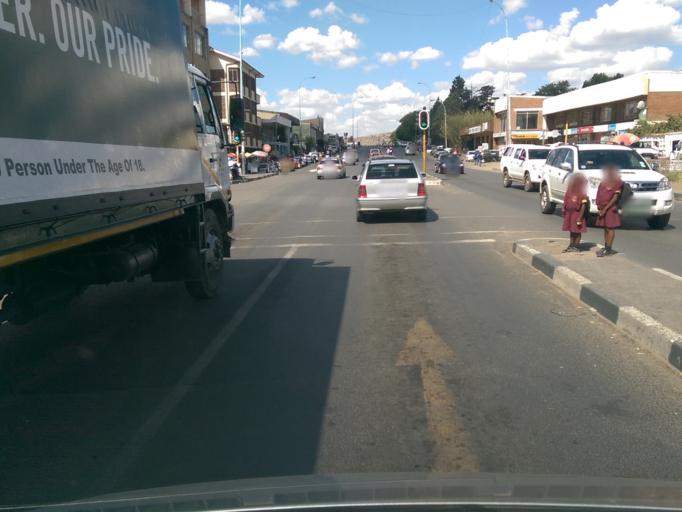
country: LS
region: Maseru
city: Maseru
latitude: -29.3157
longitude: 27.4969
